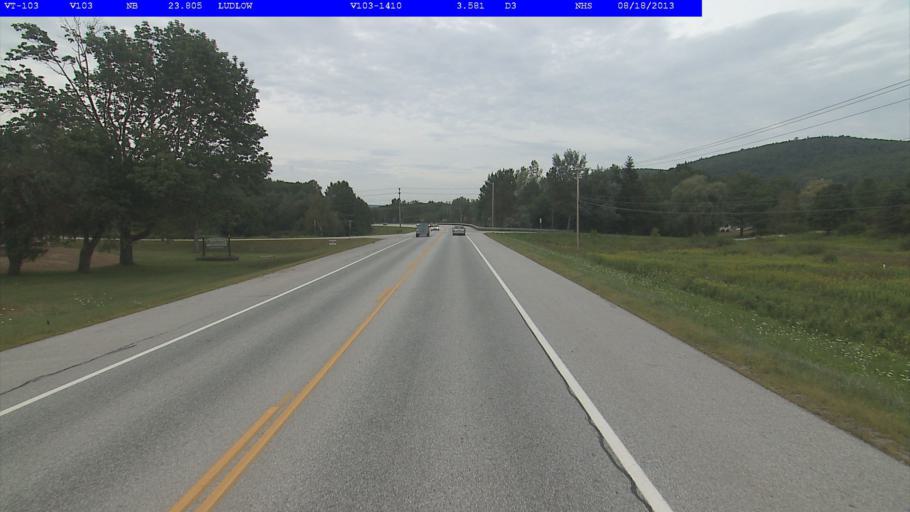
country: US
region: Vermont
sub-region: Windsor County
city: Chester
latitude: 43.4136
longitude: -72.7055
